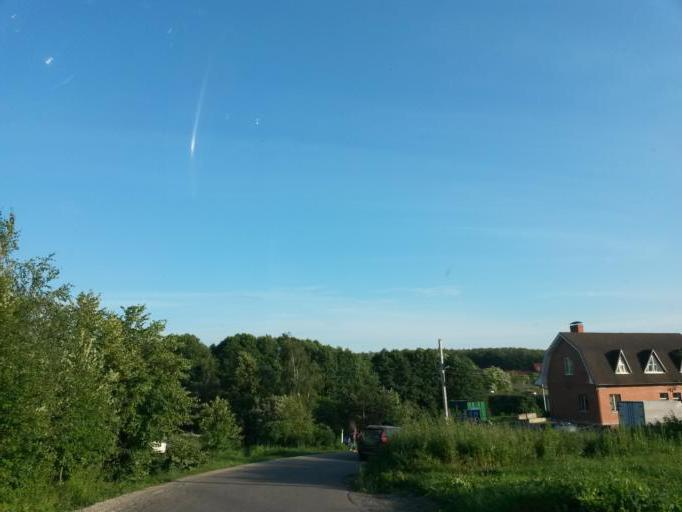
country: RU
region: Moskovskaya
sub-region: Podol'skiy Rayon
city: Podol'sk
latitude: 55.3897
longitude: 37.6209
